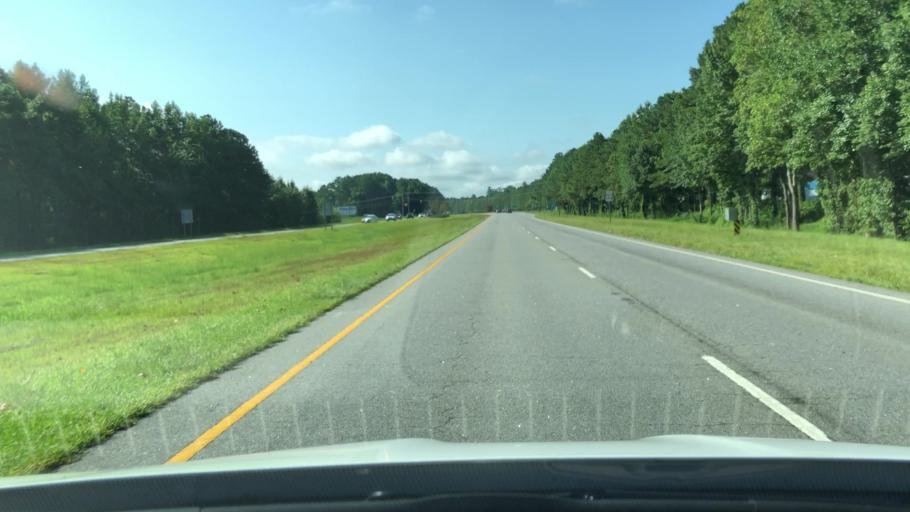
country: US
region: North Carolina
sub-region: Pasquotank County
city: Elizabeth City
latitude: 36.4177
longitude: -76.3417
